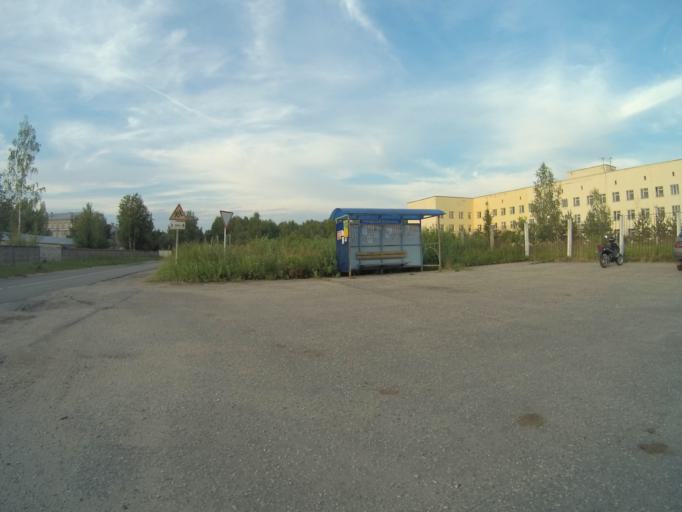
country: RU
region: Vladimir
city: Raduzhnyy
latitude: 56.0035
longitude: 40.2958
